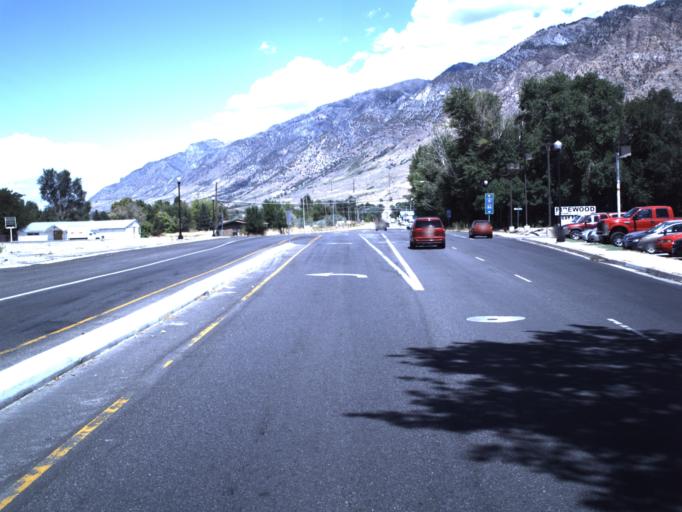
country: US
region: Utah
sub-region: Box Elder County
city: Brigham City
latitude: 41.5272
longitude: -112.0155
